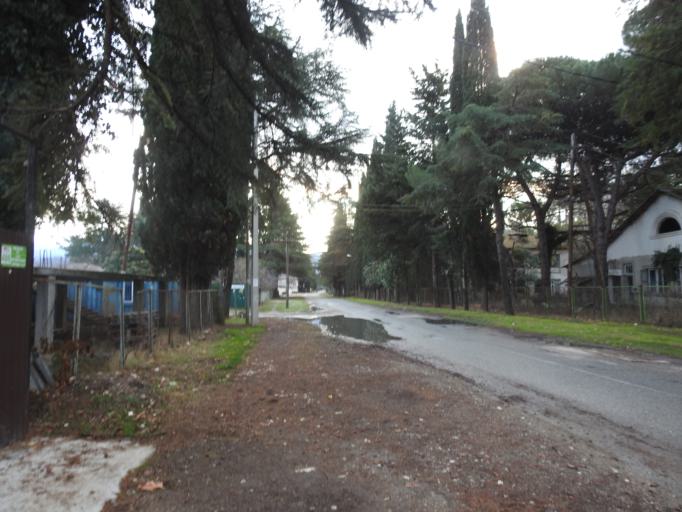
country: GE
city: Gantiadi
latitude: 43.3829
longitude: 40.0348
